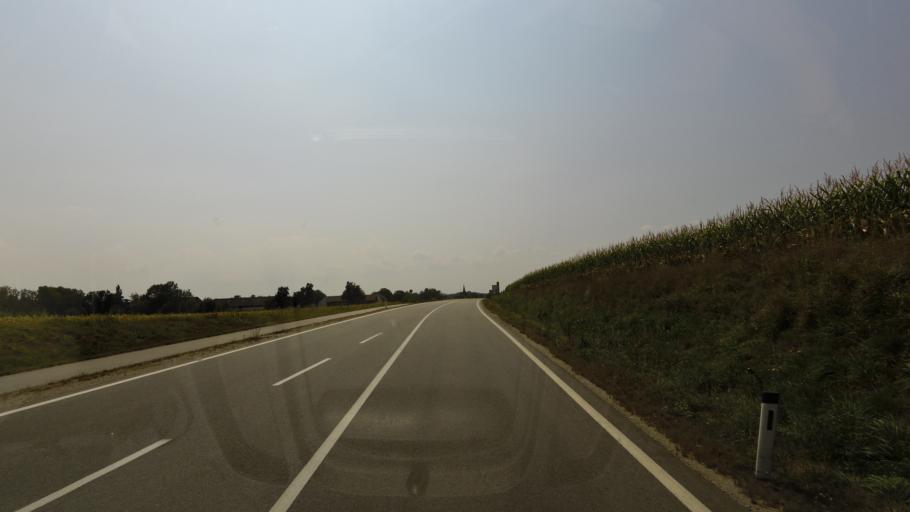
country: DE
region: Bavaria
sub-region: Lower Bavaria
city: Bad Fussing
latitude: 48.3009
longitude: 13.3319
